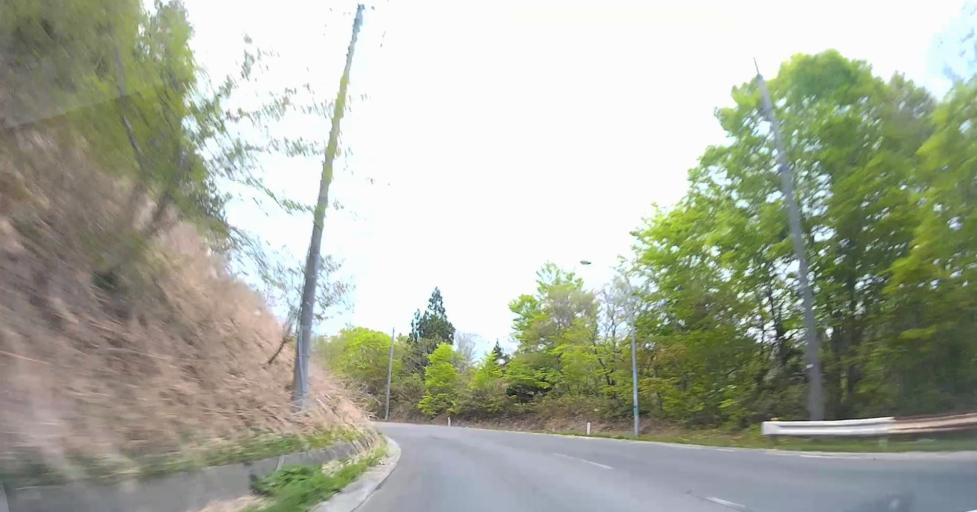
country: JP
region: Aomori
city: Goshogawara
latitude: 41.1087
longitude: 140.5355
